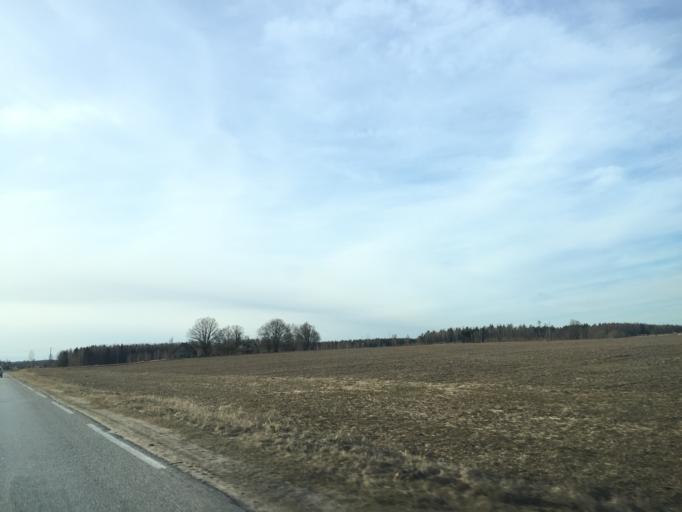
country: LV
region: Krimulda
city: Ragana
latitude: 57.1675
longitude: 24.7421
